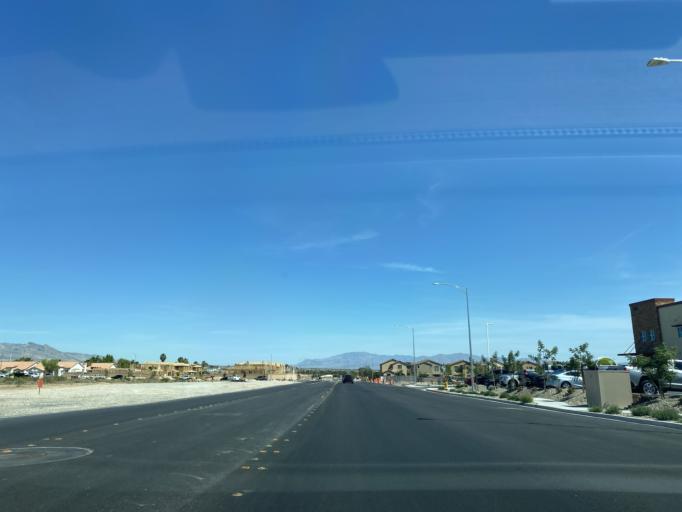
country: US
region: Nevada
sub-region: Clark County
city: Spring Valley
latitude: 36.0794
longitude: -115.2608
